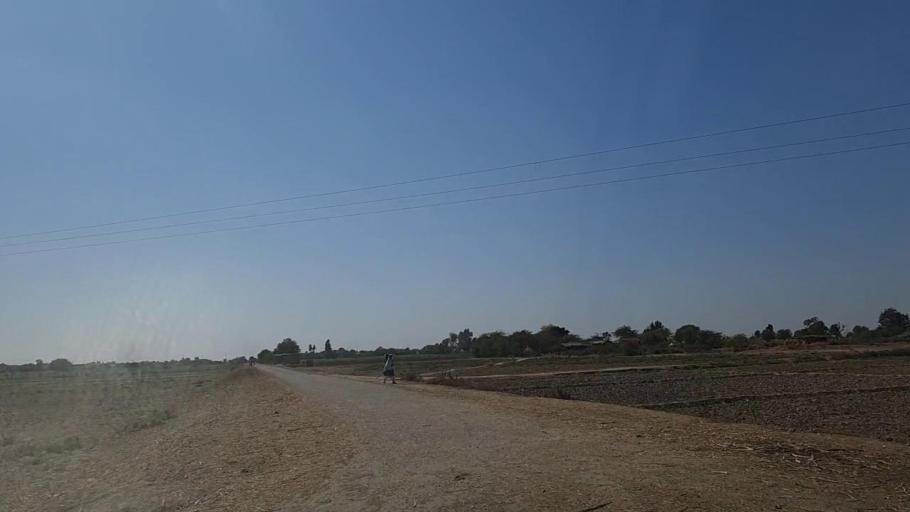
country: PK
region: Sindh
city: Naukot
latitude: 25.0624
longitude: 69.3914
